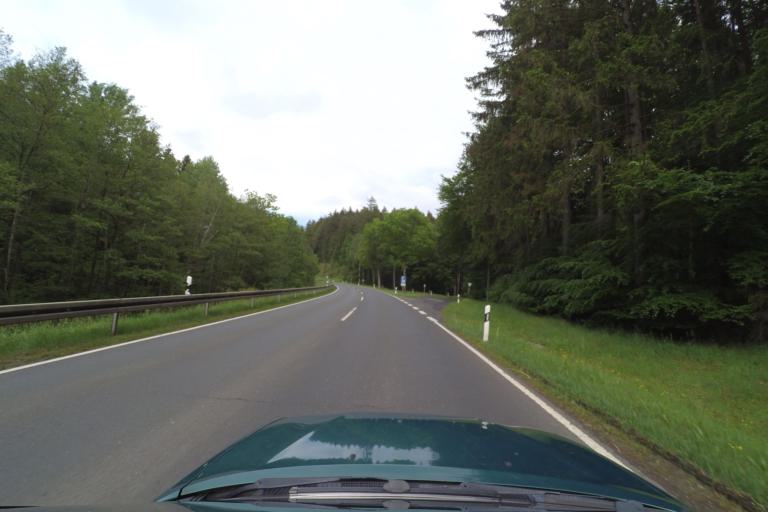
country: DE
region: Bavaria
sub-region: Upper Palatinate
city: Theisseil
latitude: 49.6813
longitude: 12.2204
